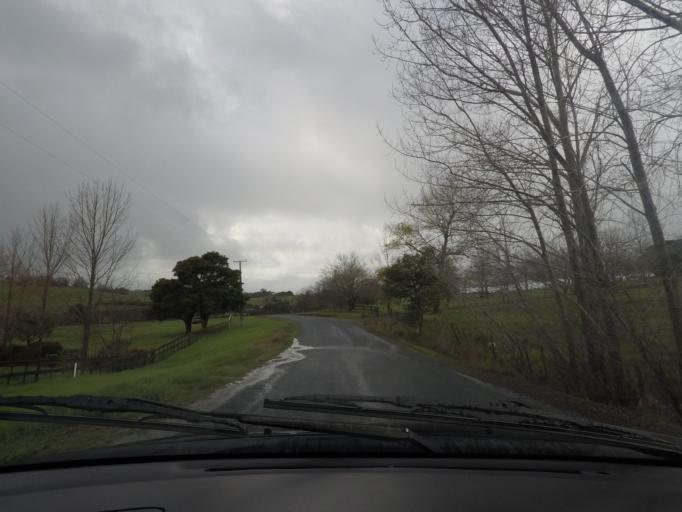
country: NZ
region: Auckland
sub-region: Auckland
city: Warkworth
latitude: -36.4354
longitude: 174.7296
